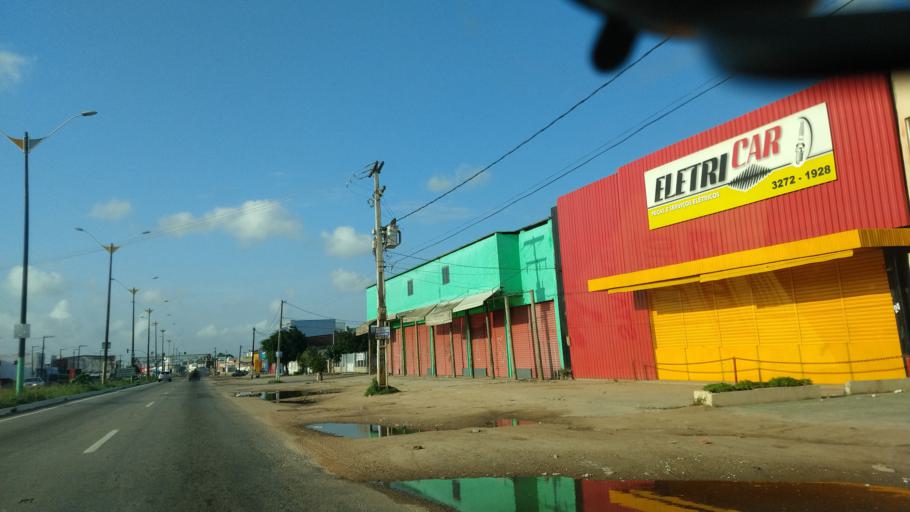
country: BR
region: Rio Grande do Norte
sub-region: Parnamirim
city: Parnamirim
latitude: -5.9194
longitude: -35.2642
